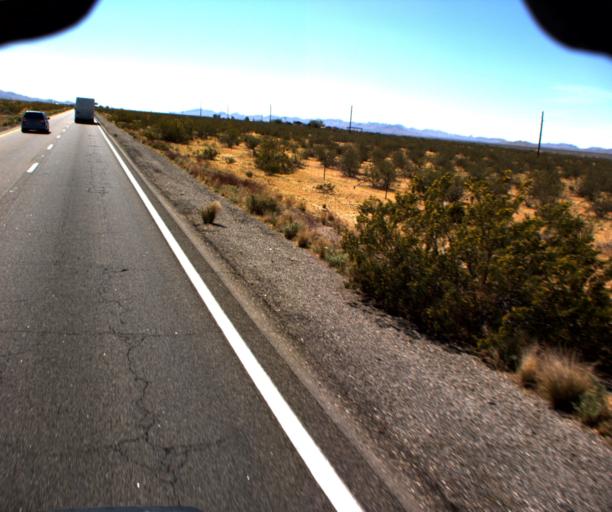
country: US
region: Arizona
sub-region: Mohave County
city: Dolan Springs
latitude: 35.5725
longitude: -114.3823
